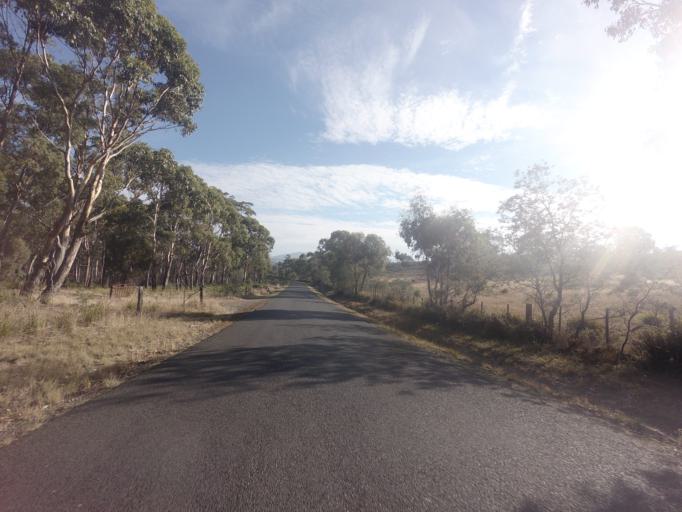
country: AU
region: Tasmania
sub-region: Brighton
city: Bridgewater
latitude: -42.5176
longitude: 147.3839
